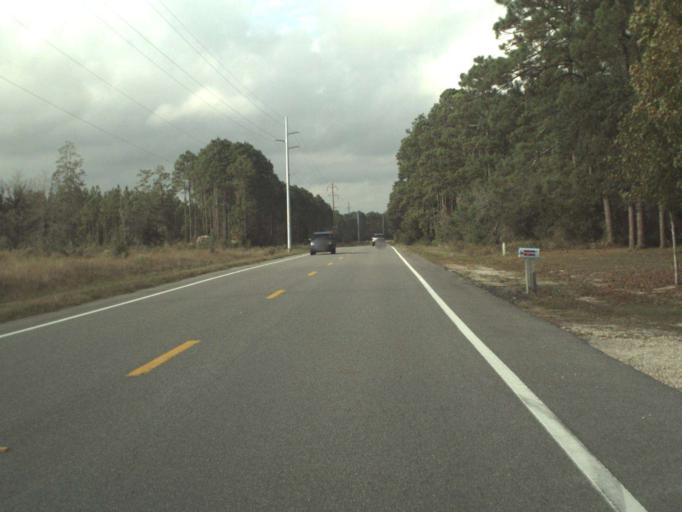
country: US
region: Florida
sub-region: Franklin County
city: Carrabelle
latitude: 29.9493
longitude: -84.5031
